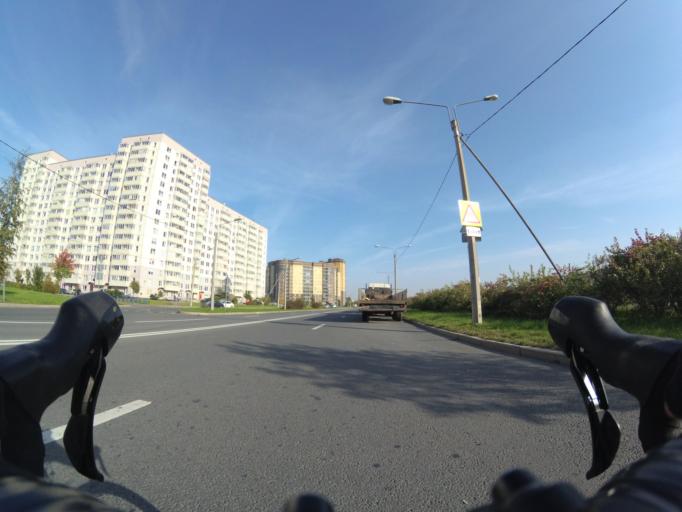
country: RU
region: Leningrad
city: Untolovo
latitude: 59.9952
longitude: 30.2087
